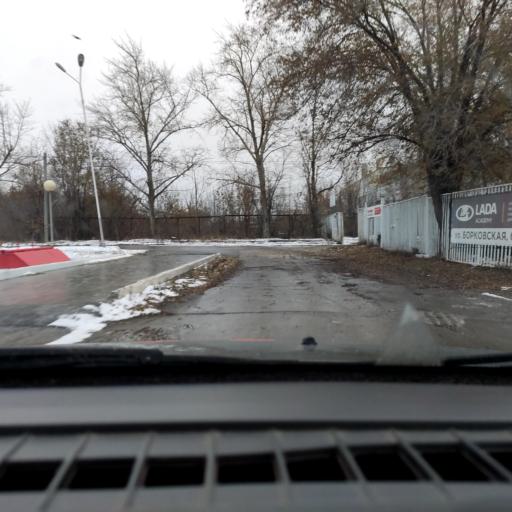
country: RU
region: Samara
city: Tol'yatti
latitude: 53.5499
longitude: 49.2826
